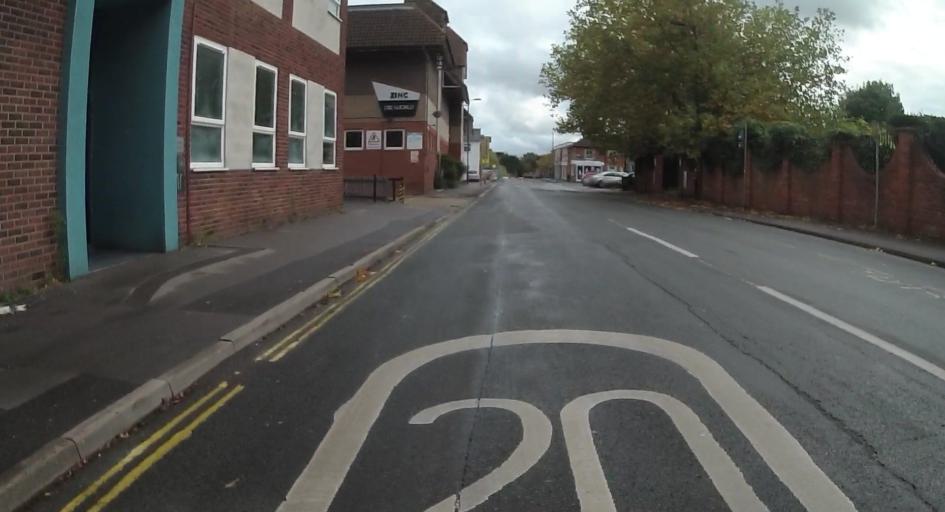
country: GB
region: England
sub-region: Hampshire
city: Fleet
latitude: 51.2801
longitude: -0.8430
